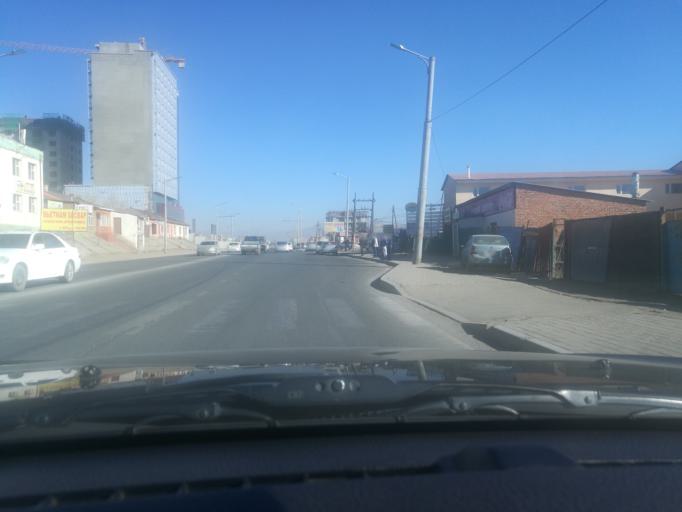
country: MN
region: Ulaanbaatar
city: Ulaanbaatar
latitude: 47.9331
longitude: 106.9061
